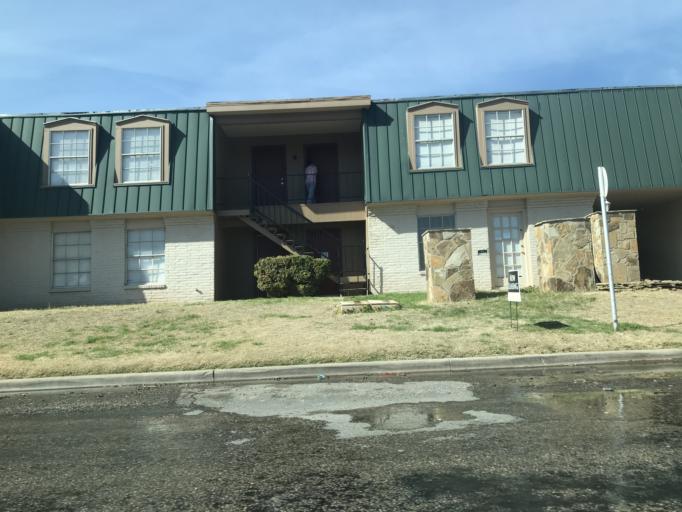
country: US
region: Texas
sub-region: Tom Green County
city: San Angelo
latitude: 31.4431
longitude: -100.4781
